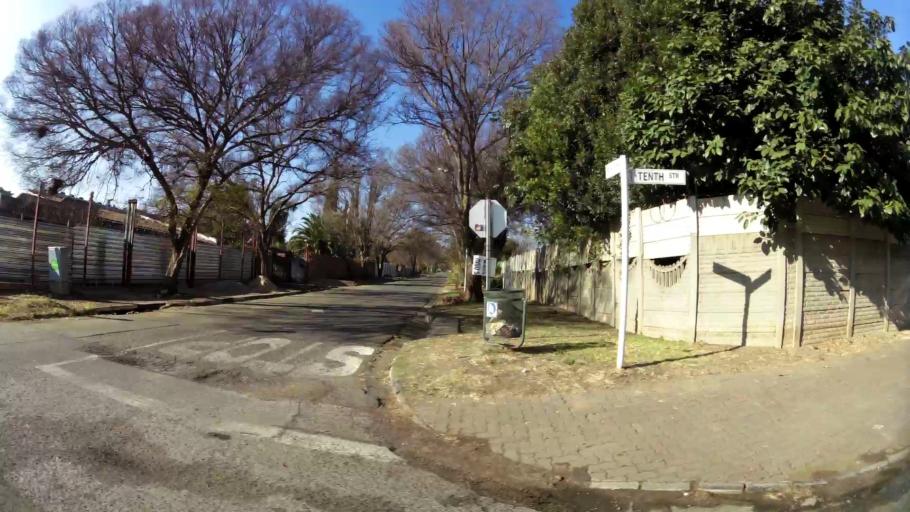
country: ZA
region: Gauteng
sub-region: City of Johannesburg Metropolitan Municipality
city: Modderfontein
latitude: -26.1334
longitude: 28.1458
